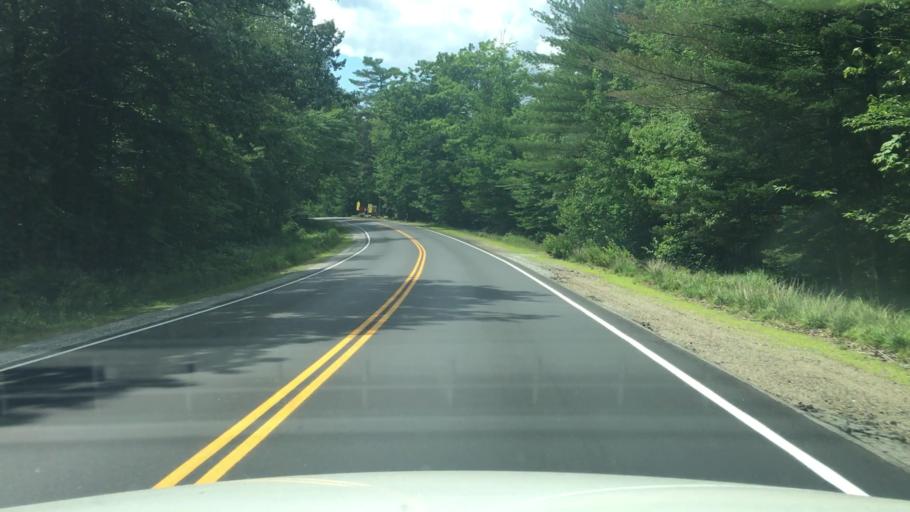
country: US
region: Maine
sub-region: Oxford County
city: Bethel
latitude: 44.3979
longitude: -70.6733
